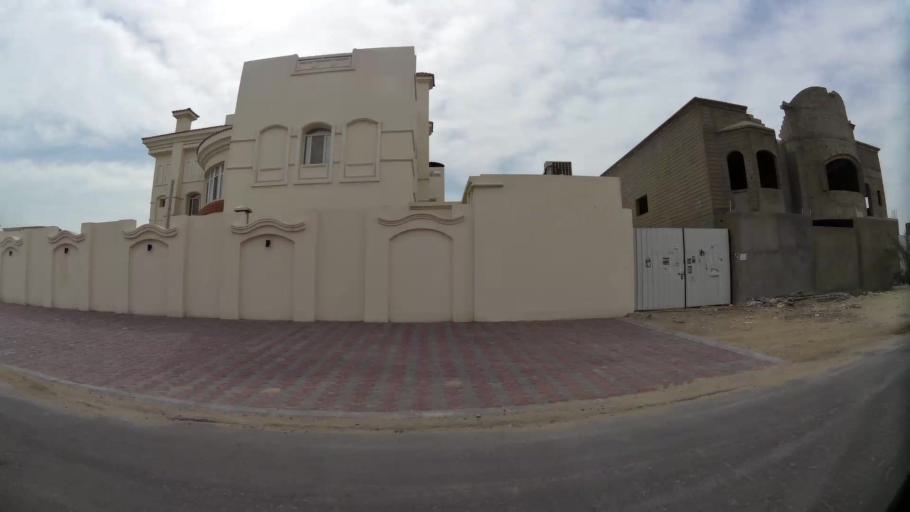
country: QA
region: Baladiyat ad Dawhah
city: Doha
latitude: 25.2132
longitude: 51.4935
